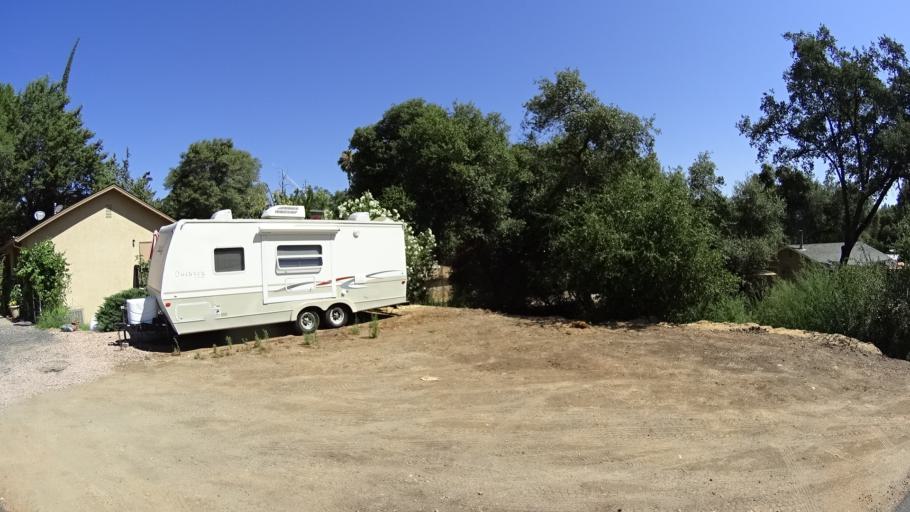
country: US
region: California
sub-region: Calaveras County
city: Angels Camp
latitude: 38.0700
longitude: -120.5454
